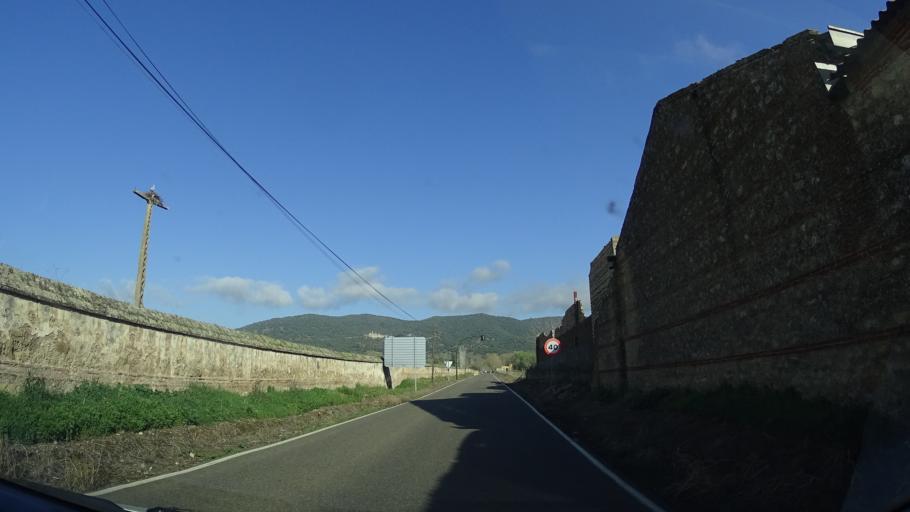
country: ES
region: Andalusia
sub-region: Province of Cordoba
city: Villarrubia
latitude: 37.8766
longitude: -4.8494
